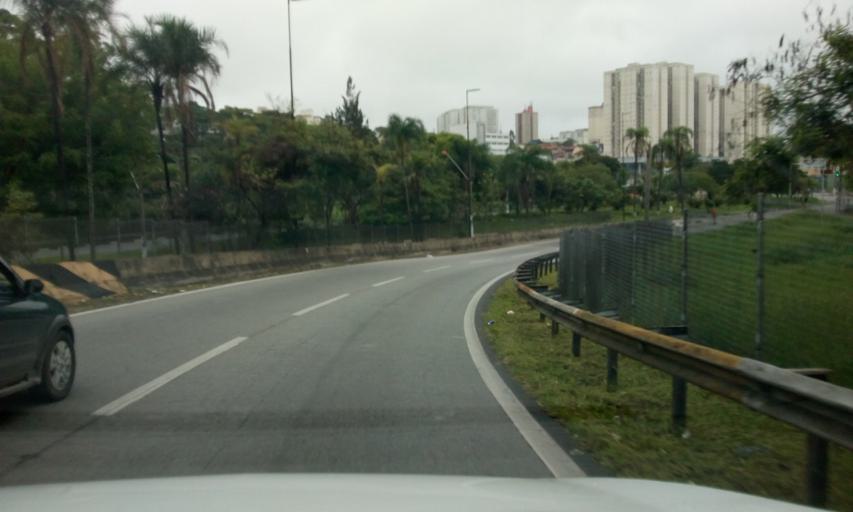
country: BR
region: Sao Paulo
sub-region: Diadema
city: Diadema
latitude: -23.6839
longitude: -46.6104
